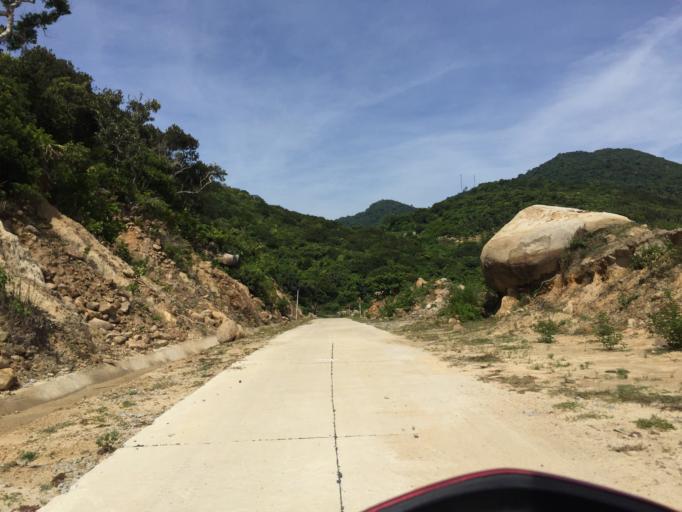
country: VN
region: Quang Nam
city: Hoi An
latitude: 15.9632
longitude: 108.5116
